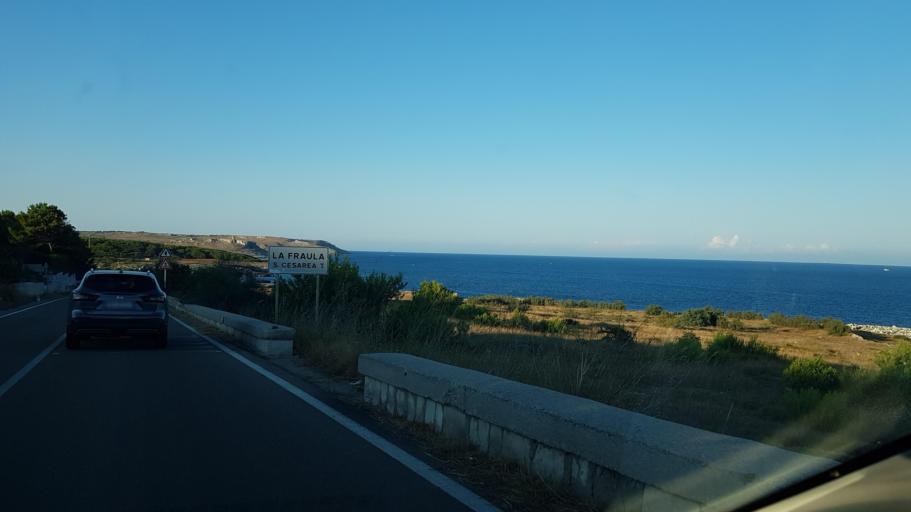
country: IT
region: Apulia
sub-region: Provincia di Lecce
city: Cerfignano
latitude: 40.0739
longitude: 18.4809
